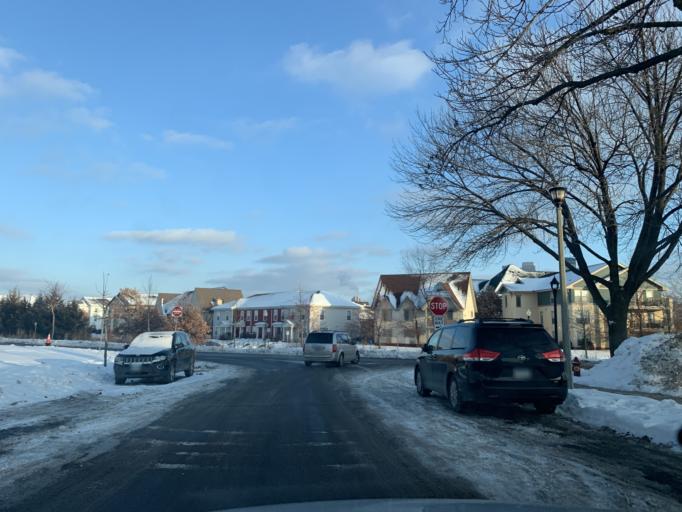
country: US
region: Minnesota
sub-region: Hennepin County
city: Minneapolis
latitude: 44.9852
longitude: -93.2944
